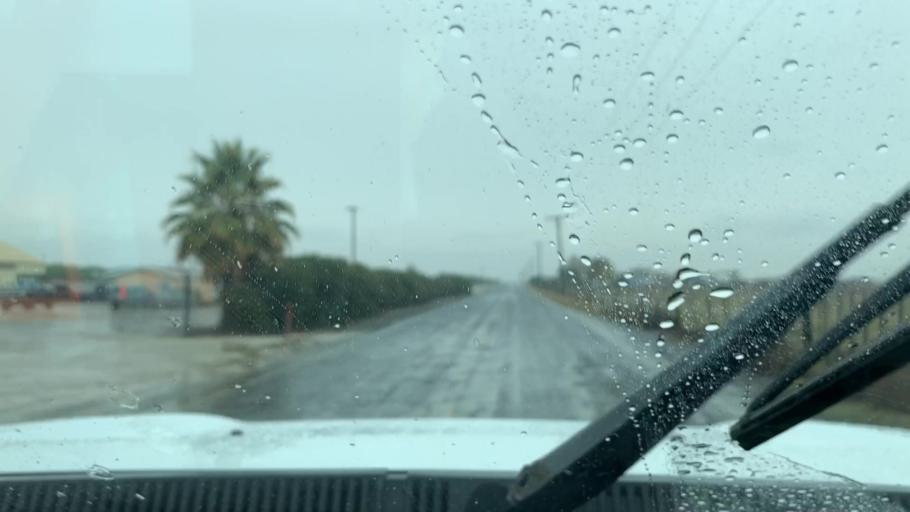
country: US
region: California
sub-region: Tulare County
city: Earlimart
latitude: 35.8919
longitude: -119.3399
